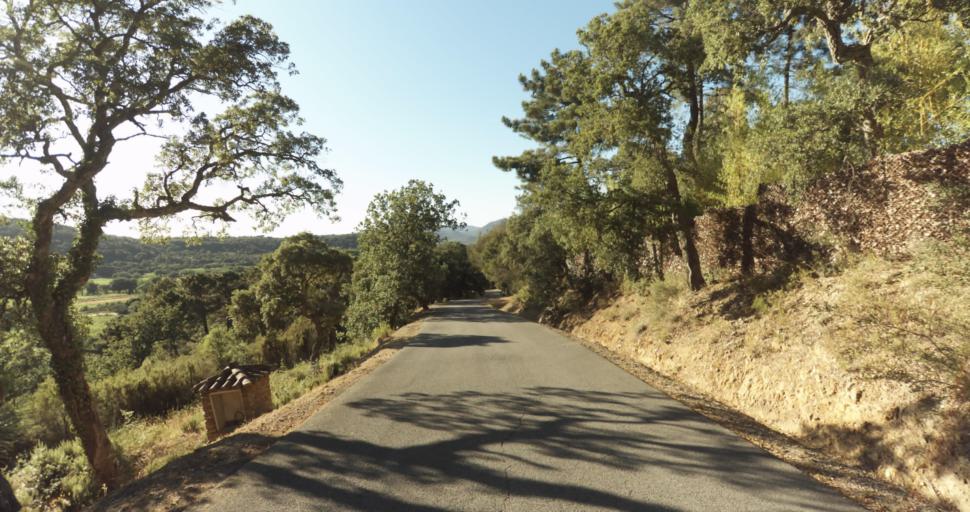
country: FR
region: Provence-Alpes-Cote d'Azur
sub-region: Departement du Var
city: Gassin
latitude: 43.2369
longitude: 6.5975
